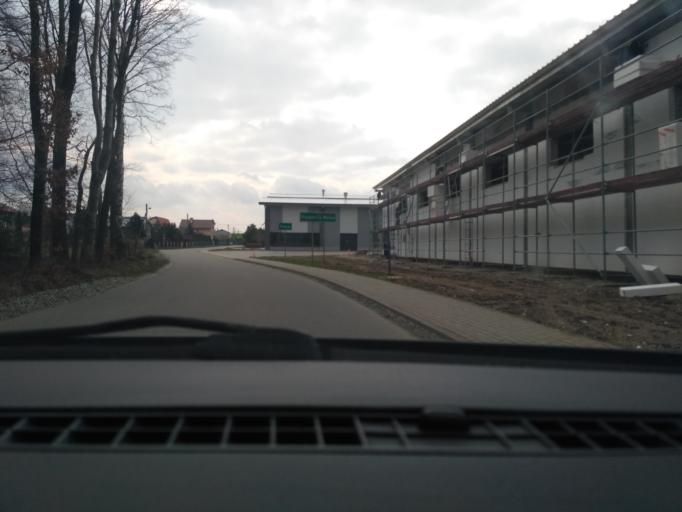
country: PL
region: Subcarpathian Voivodeship
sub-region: Powiat krosnienski
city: Kroscienko Wyzne
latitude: 49.6666
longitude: 21.8307
